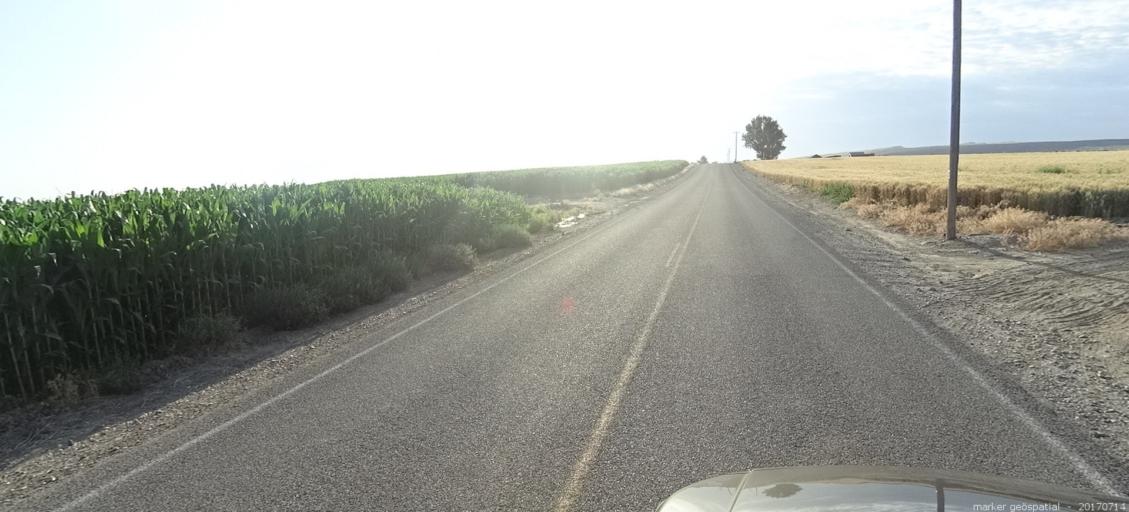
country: US
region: Idaho
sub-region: Ada County
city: Kuna
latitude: 43.4593
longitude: -116.5109
